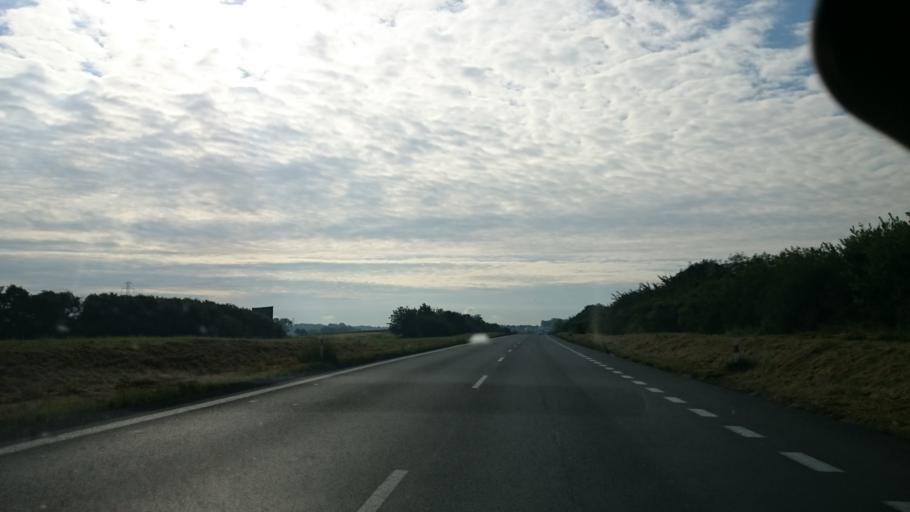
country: PL
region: Opole Voivodeship
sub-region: Powiat opolski
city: Opole
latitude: 50.7020
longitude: 17.9436
